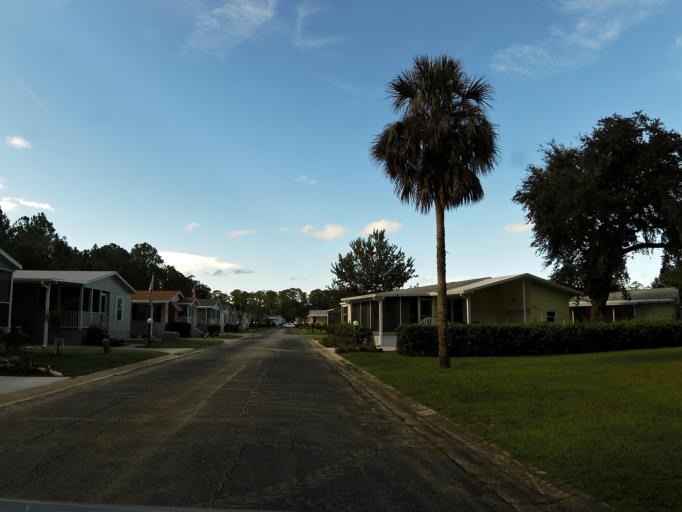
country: US
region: Florida
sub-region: Flagler County
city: Bunnell
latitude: 29.4605
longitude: -81.2631
